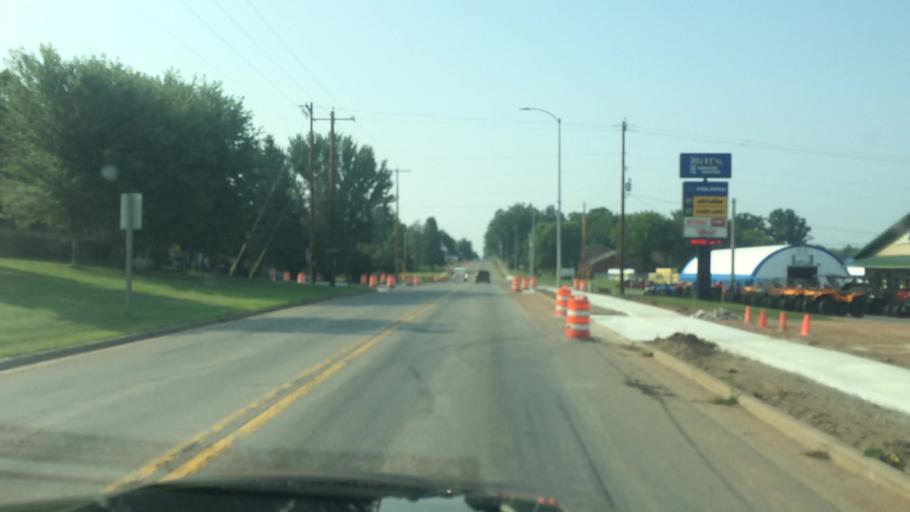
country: US
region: Wisconsin
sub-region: Marathon County
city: Stratford
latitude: 44.8088
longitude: -90.0792
